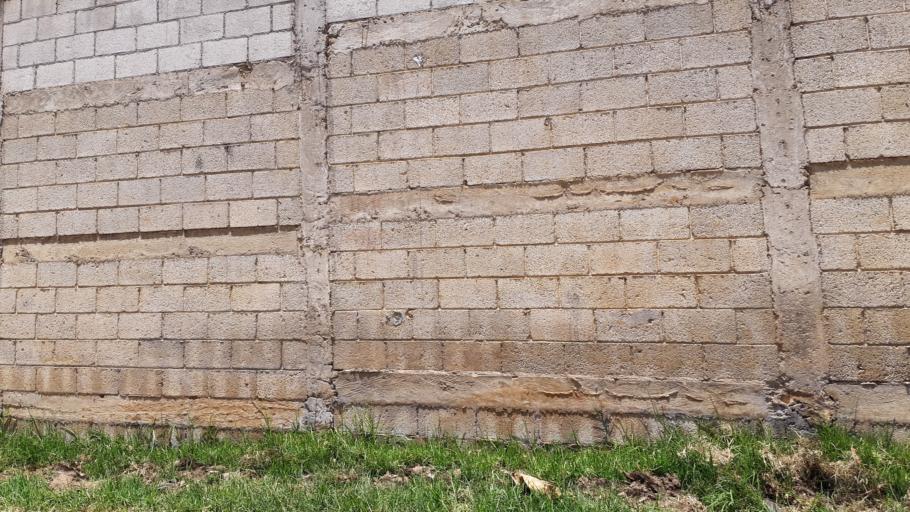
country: GT
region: Chimaltenango
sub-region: Municipio de Chimaltenango
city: Chimaltenango
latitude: 14.6629
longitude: -90.8422
